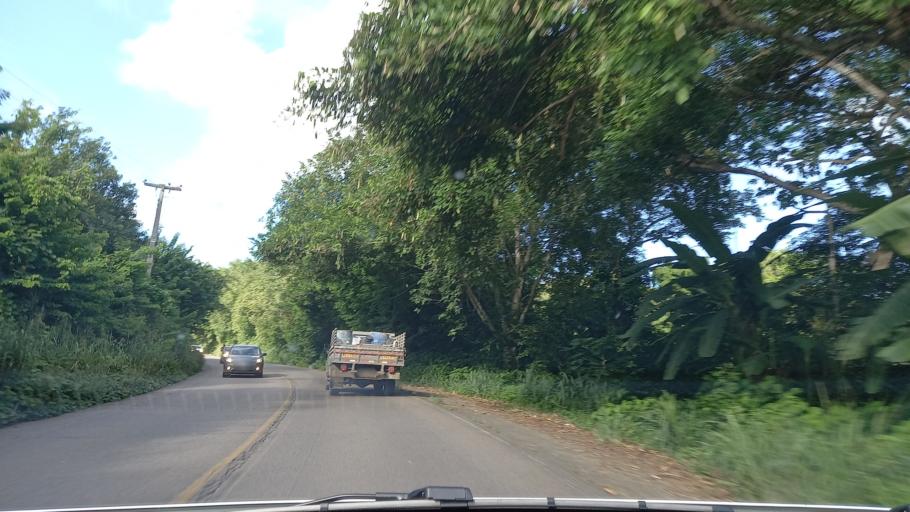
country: BR
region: Pernambuco
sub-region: Rio Formoso
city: Rio Formoso
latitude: -8.6577
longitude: -35.1429
